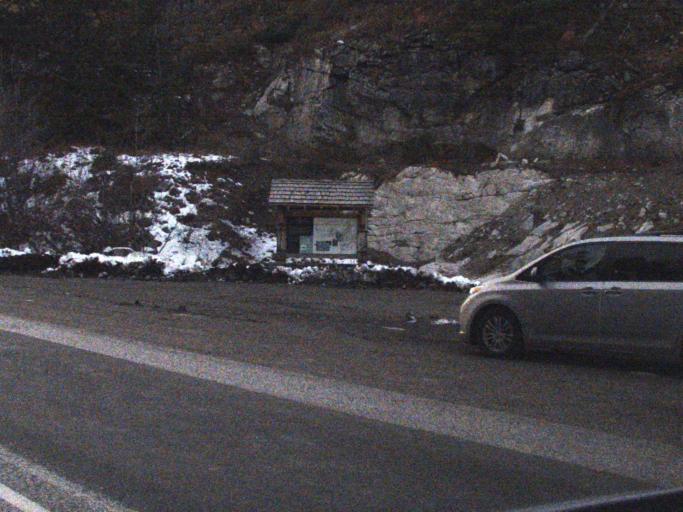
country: US
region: Washington
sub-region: Ferry County
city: Republic
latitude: 48.6072
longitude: -118.4792
